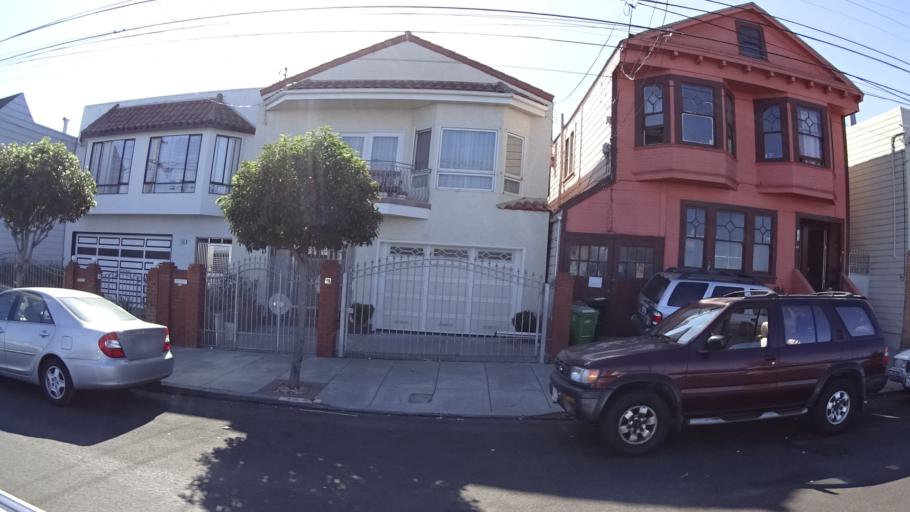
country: US
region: California
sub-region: San Francisco County
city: San Francisco
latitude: 37.7289
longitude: -122.4107
